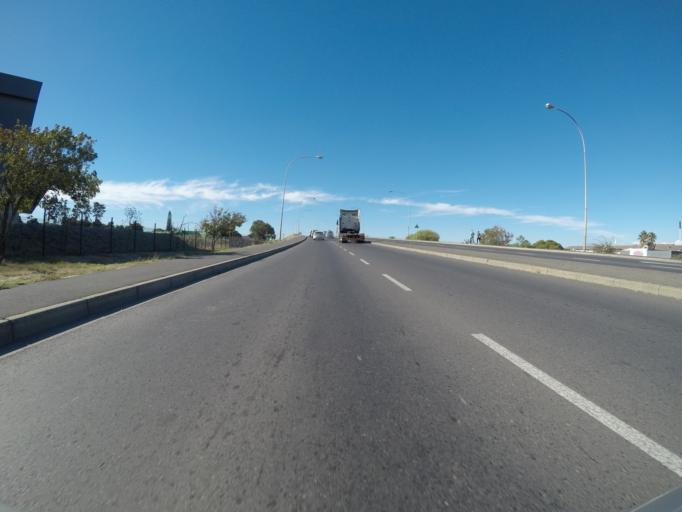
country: ZA
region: Western Cape
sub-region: City of Cape Town
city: Kraaifontein
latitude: -33.8950
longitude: 18.6722
